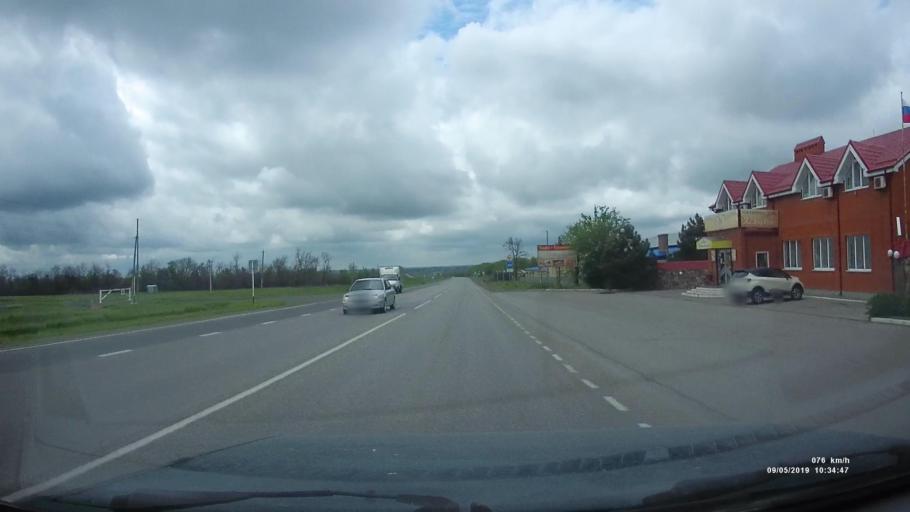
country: RU
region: Rostov
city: Peshkovo
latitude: 47.0503
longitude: 39.4170
